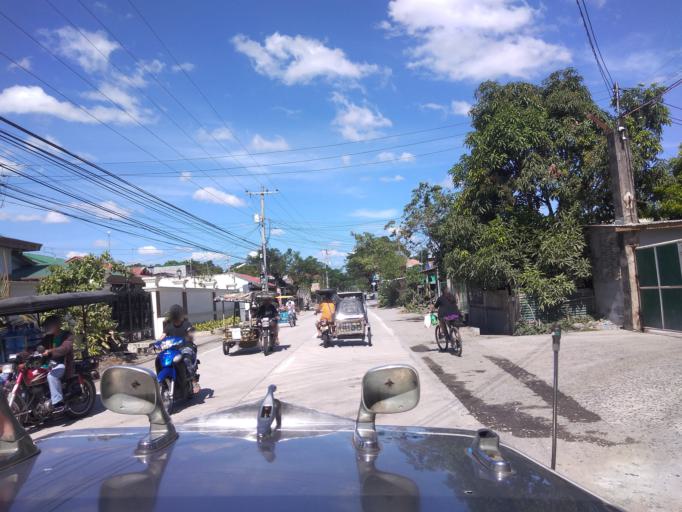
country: PH
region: Central Luzon
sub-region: Province of Pampanga
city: Santa Rita
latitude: 14.9999
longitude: 120.6115
